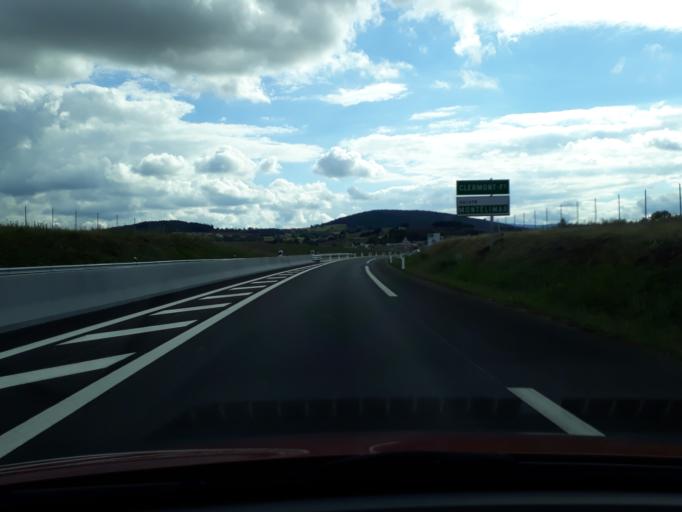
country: FR
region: Auvergne
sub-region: Departement de la Haute-Loire
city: Cussac-sur-Loire
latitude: 45.0019
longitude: 3.8789
